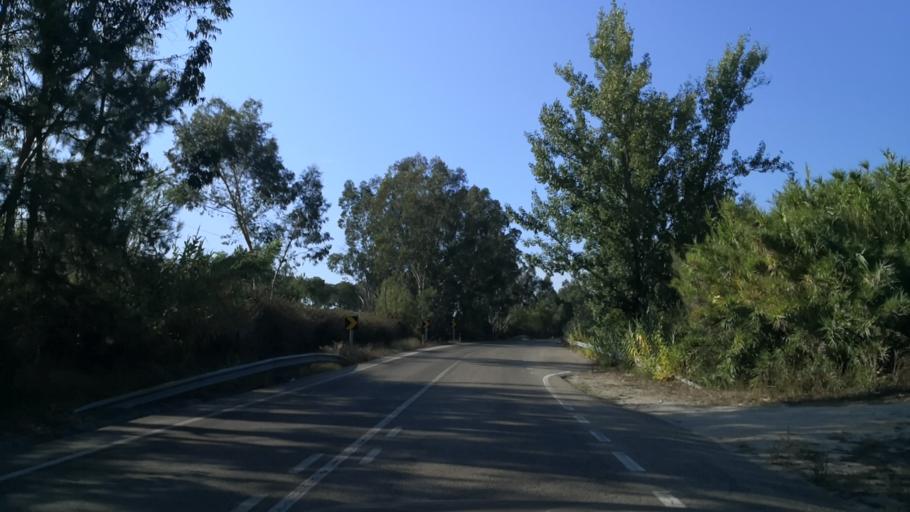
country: PT
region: Santarem
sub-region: Almeirim
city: Fazendas de Almeirim
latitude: 39.0874
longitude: -8.5721
